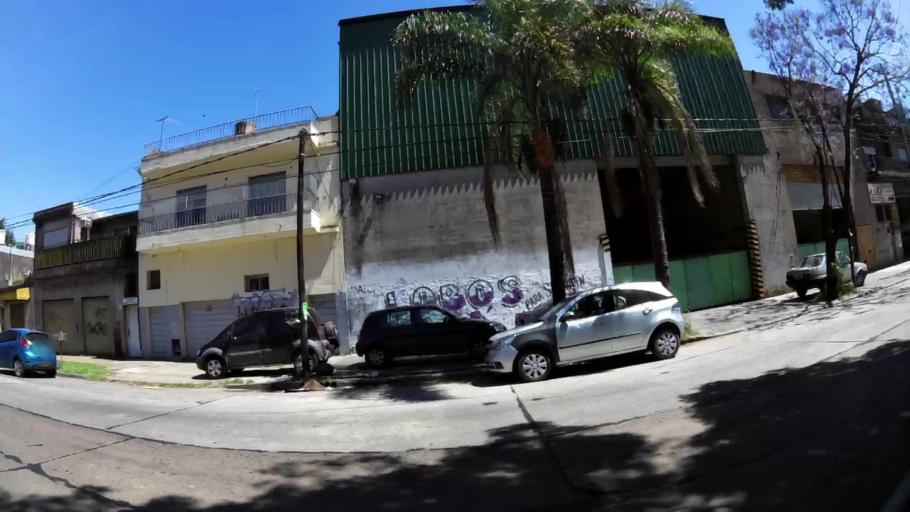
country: AR
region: Buenos Aires
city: Caseros
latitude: -34.5868
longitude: -58.5607
